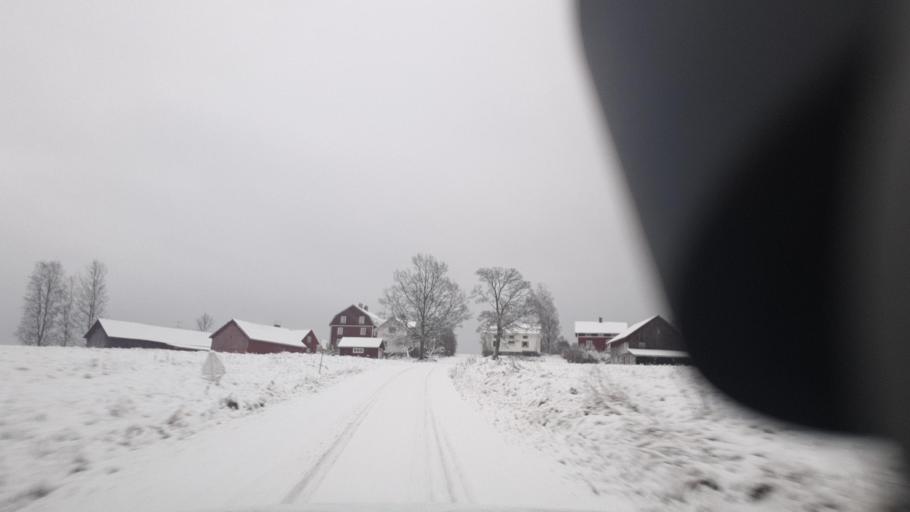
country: SE
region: Vaermland
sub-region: Eda Kommun
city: Amotfors
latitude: 59.7307
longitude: 12.1942
